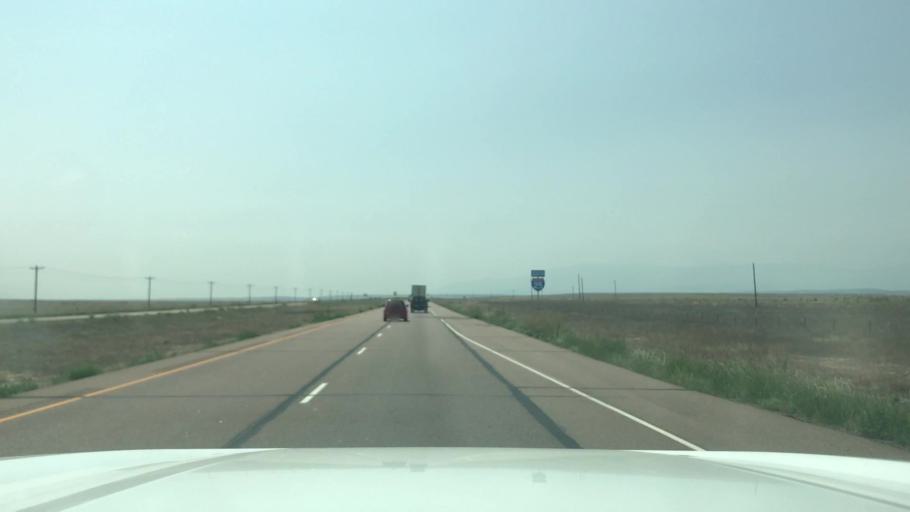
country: US
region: Colorado
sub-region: Pueblo County
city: Pueblo
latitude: 38.1566
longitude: -104.6479
